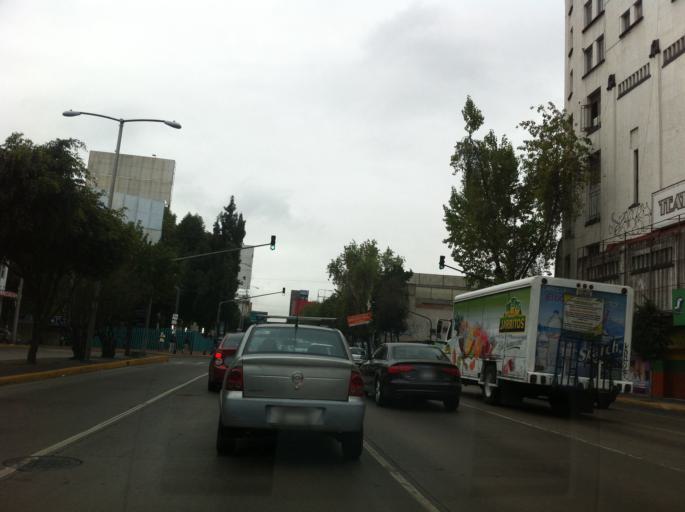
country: MX
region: Mexico City
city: Polanco
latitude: 19.4073
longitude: -99.1843
